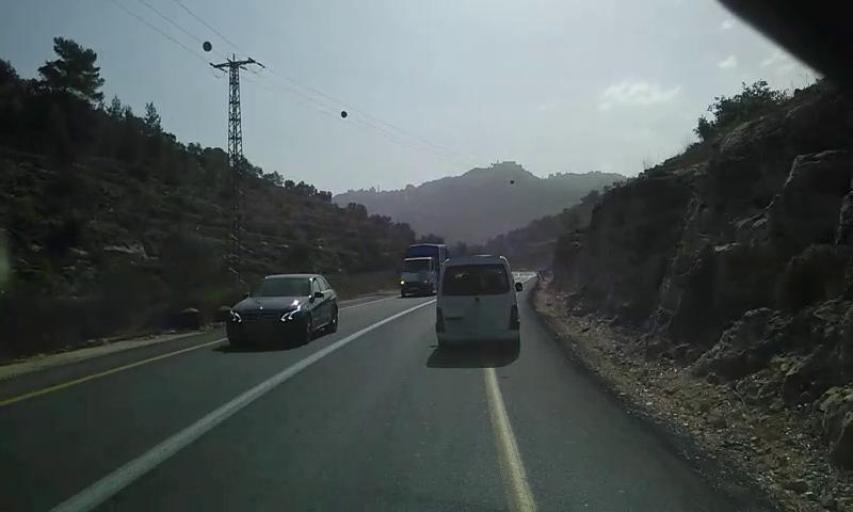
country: PS
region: West Bank
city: Silwad
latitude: 31.9946
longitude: 35.2444
